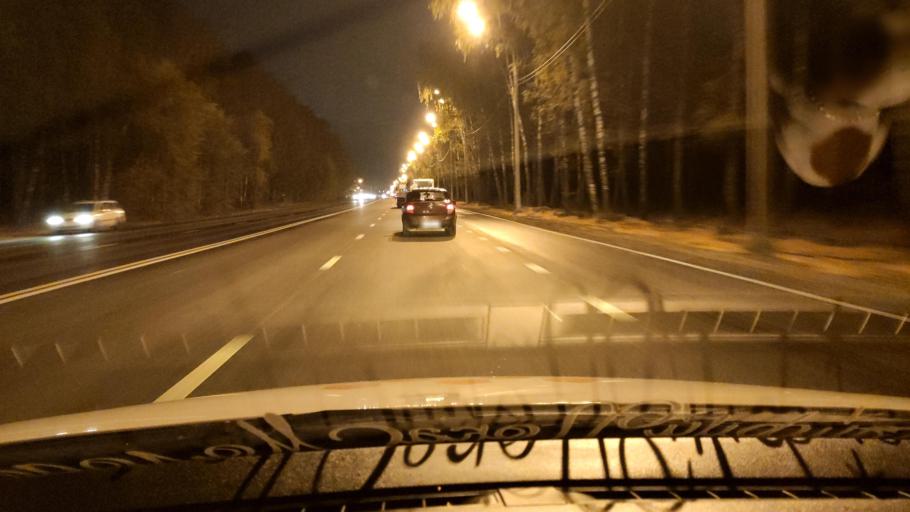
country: RU
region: Voronezj
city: Pridonskoy
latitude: 51.6912
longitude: 39.0991
